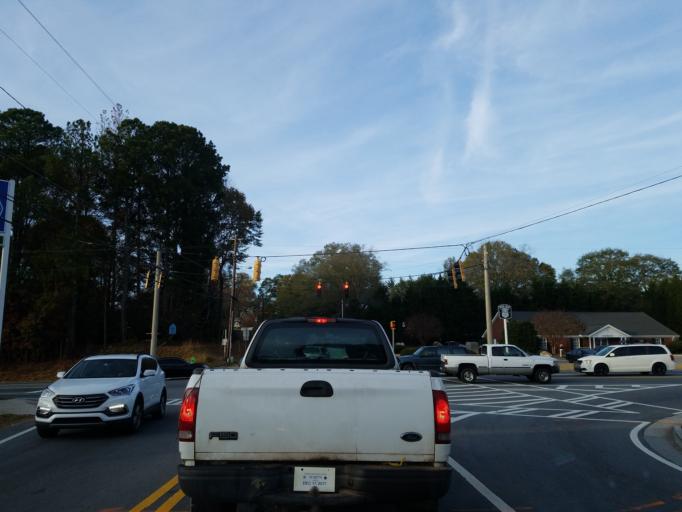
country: US
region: Georgia
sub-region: Carroll County
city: Temple
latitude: 33.7307
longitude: -85.0289
